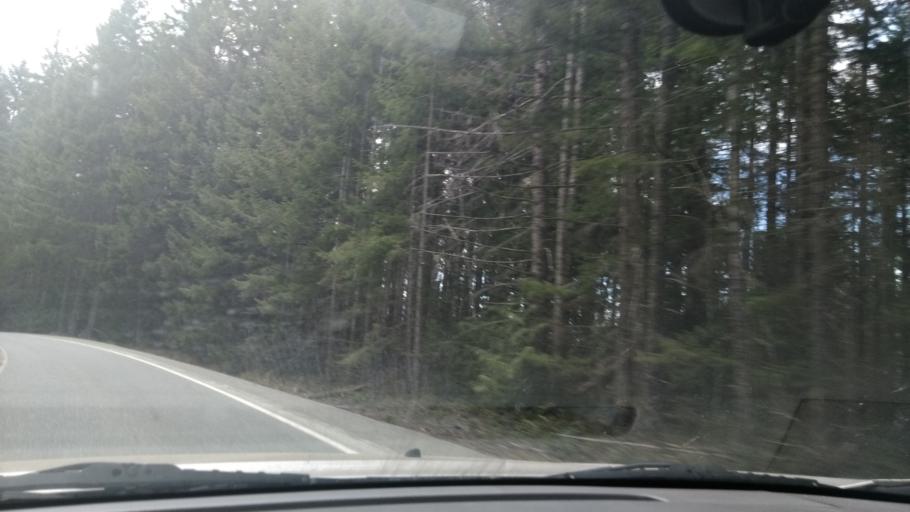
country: CA
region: British Columbia
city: Campbell River
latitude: 49.8713
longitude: -125.6538
